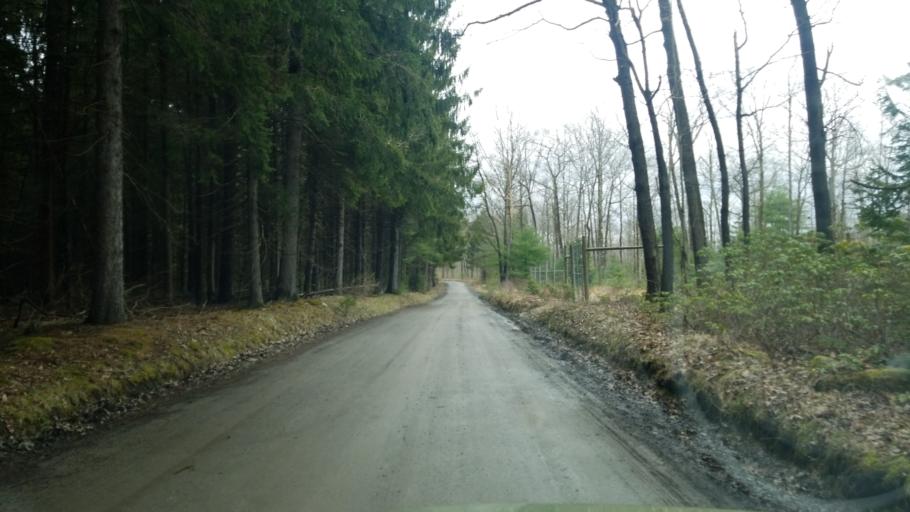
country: US
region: Pennsylvania
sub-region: Clearfield County
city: Shiloh
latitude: 41.1686
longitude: -78.2714
